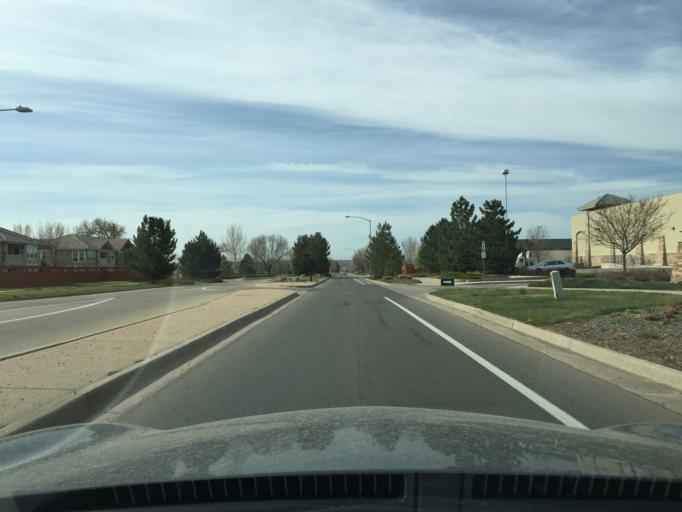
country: US
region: Colorado
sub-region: Broomfield County
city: Broomfield
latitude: 39.9573
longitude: -105.0344
